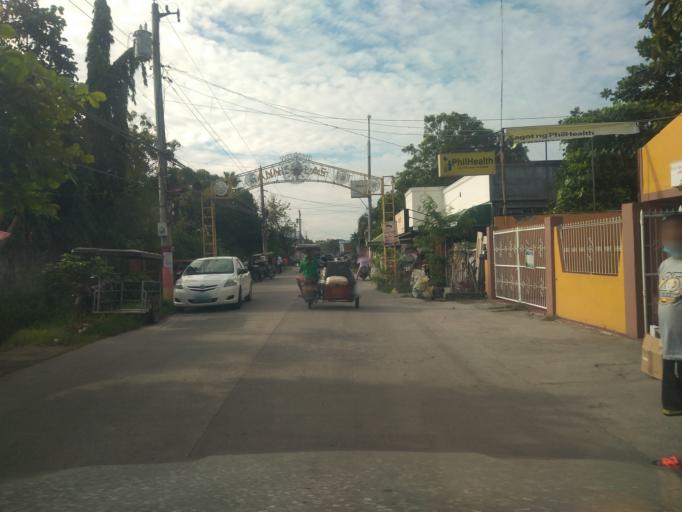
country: PH
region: Central Luzon
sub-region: Province of Pampanga
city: Sexmoan
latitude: 14.9428
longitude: 120.6219
